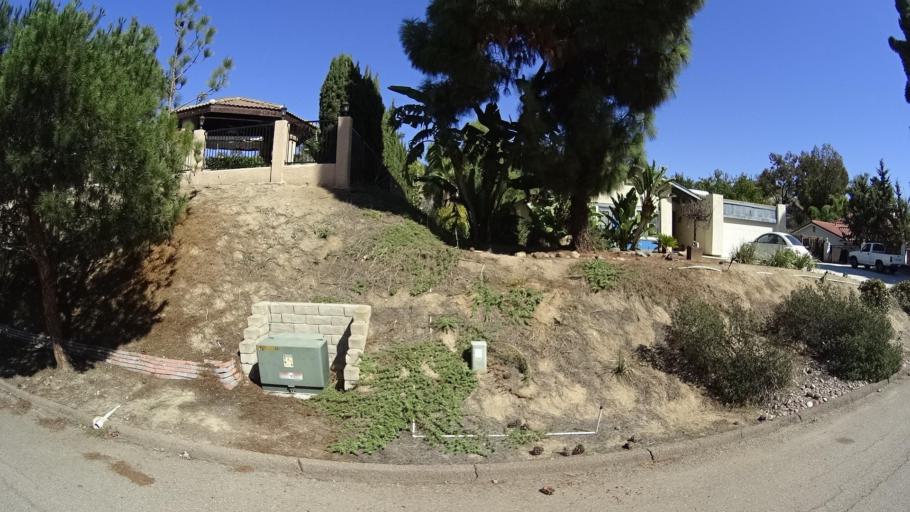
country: US
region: California
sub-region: San Diego County
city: Bonita
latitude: 32.6602
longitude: -117.0178
